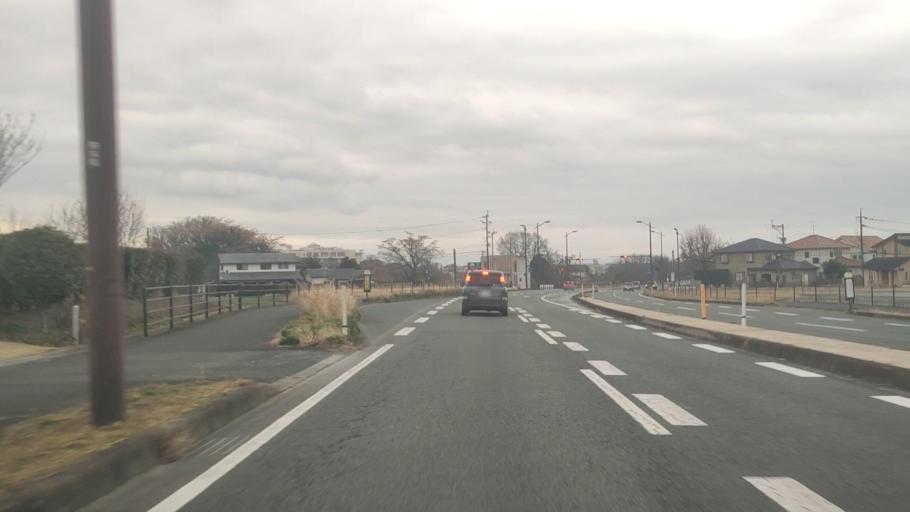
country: JP
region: Kumamoto
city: Ozu
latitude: 32.8228
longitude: 130.7911
